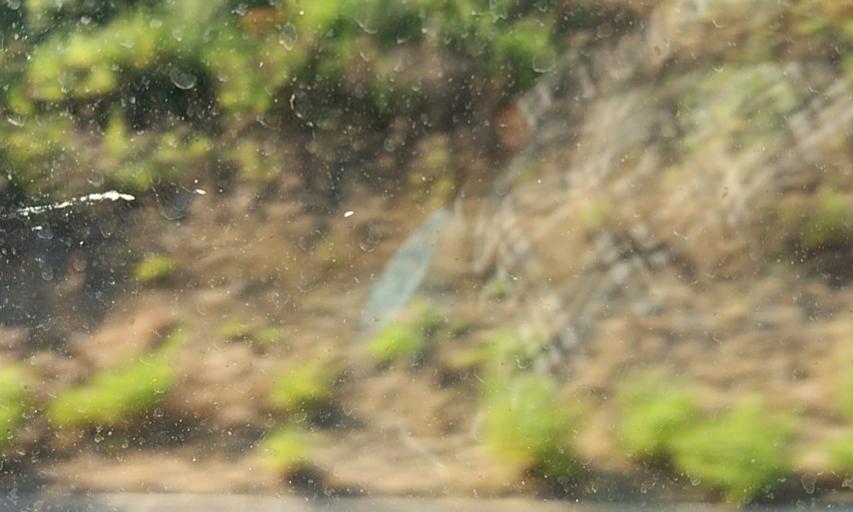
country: PT
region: Vila Real
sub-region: Murca
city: Murca
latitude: 41.4067
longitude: -7.4255
